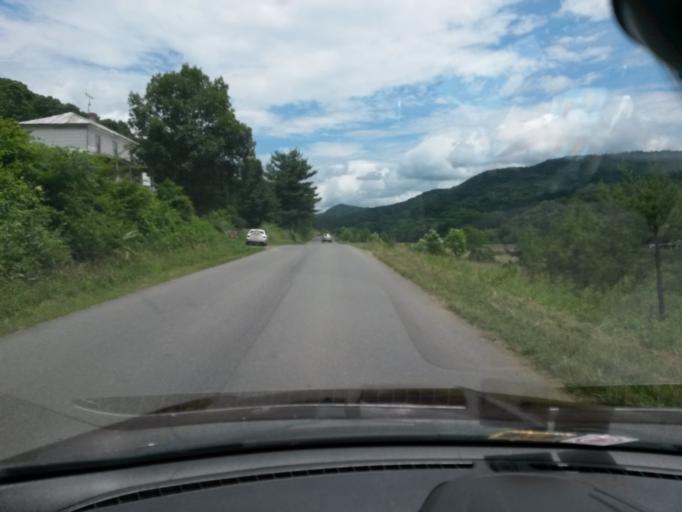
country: US
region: West Virginia
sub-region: Monroe County
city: Union
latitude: 37.5001
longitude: -80.5970
